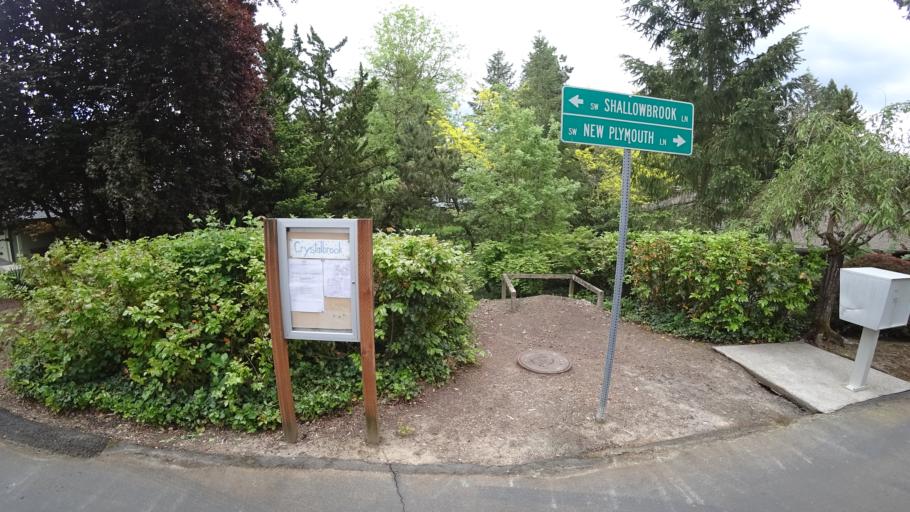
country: US
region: Oregon
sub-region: Washington County
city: Beaverton
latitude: 45.4760
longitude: -122.8331
